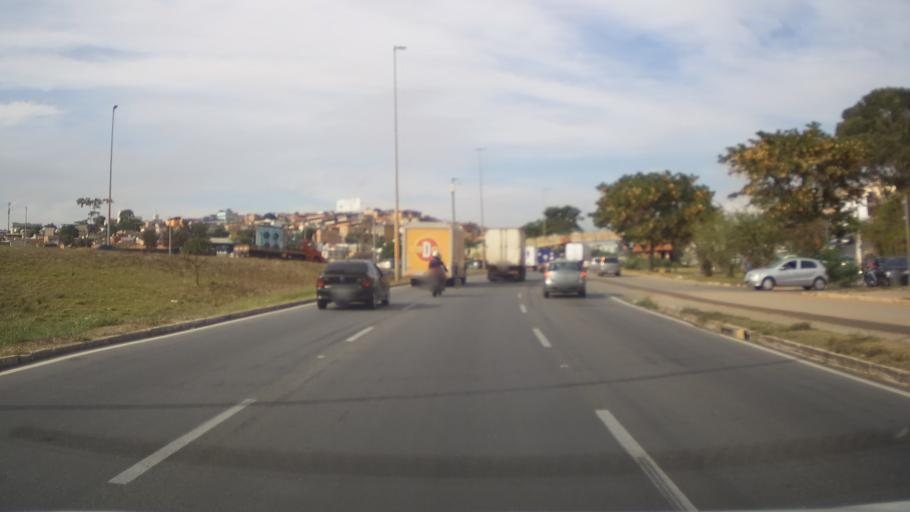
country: BR
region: Minas Gerais
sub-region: Contagem
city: Contagem
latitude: -19.9168
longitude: -44.0556
